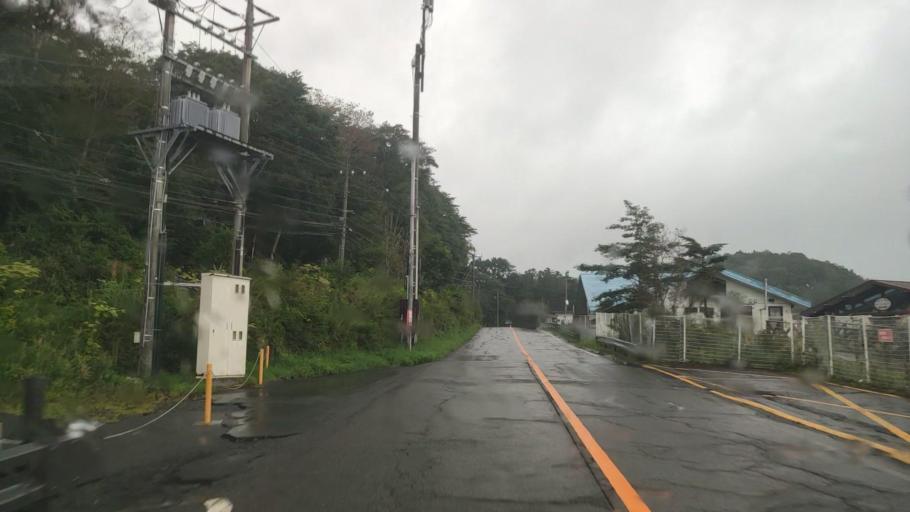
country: JP
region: Shizuoka
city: Fuji
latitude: 35.2995
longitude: 138.7680
